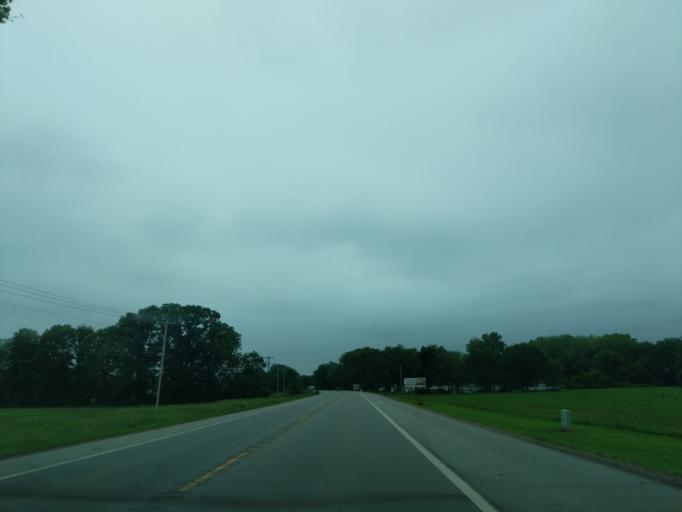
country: US
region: Michigan
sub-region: Branch County
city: Quincy
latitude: 41.9491
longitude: -84.8580
